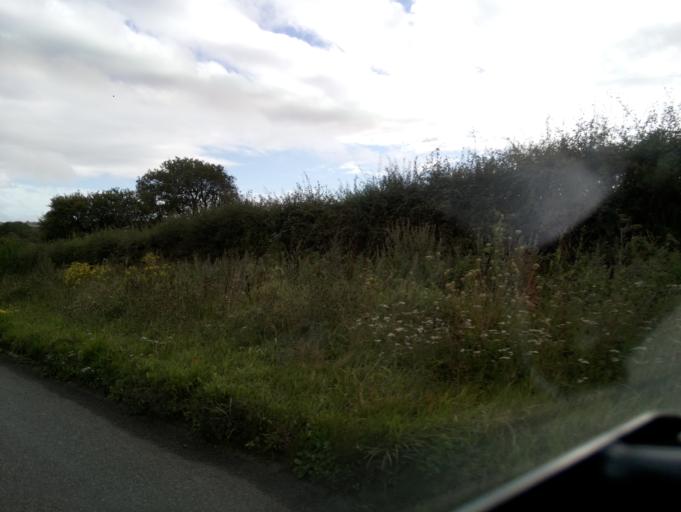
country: GB
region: England
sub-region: Devon
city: Modbury
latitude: 50.3190
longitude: -3.8405
